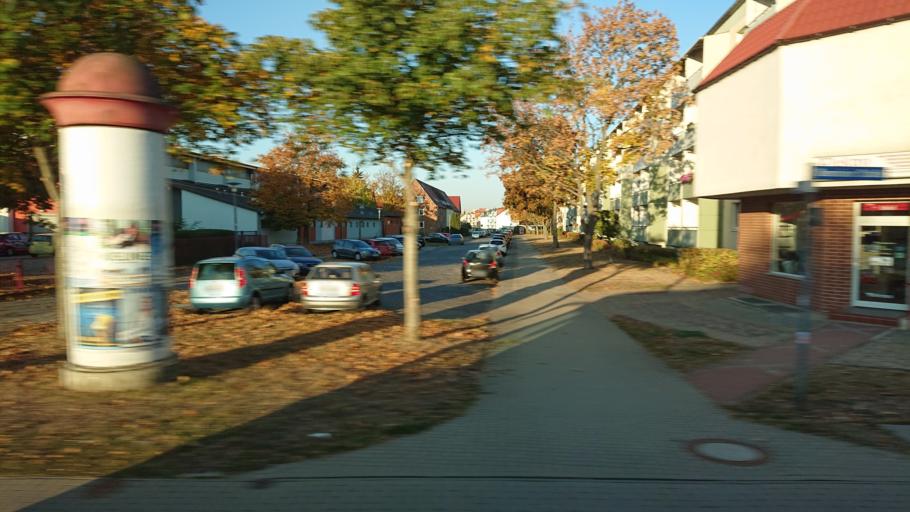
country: DE
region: Mecklenburg-Vorpommern
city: Neubrandenburg
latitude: 53.5673
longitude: 13.2694
